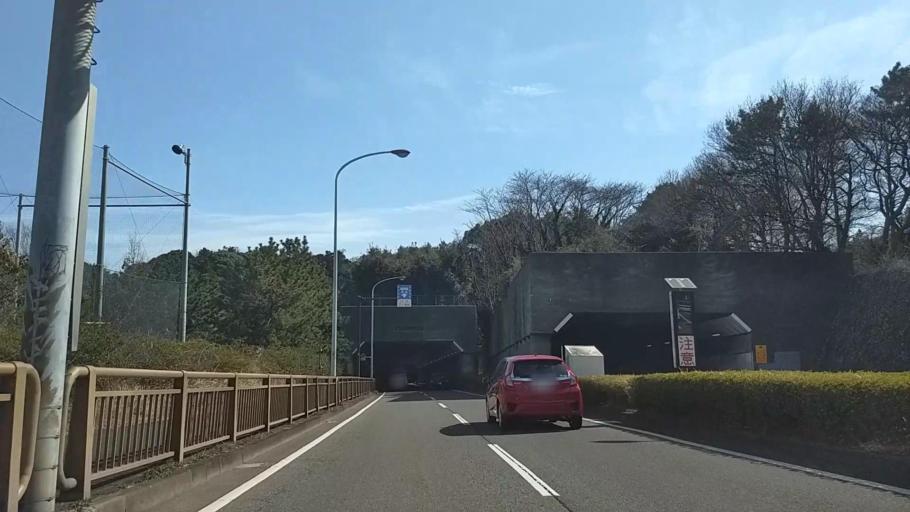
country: JP
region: Kanagawa
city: Fujisawa
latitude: 35.3526
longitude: 139.4443
